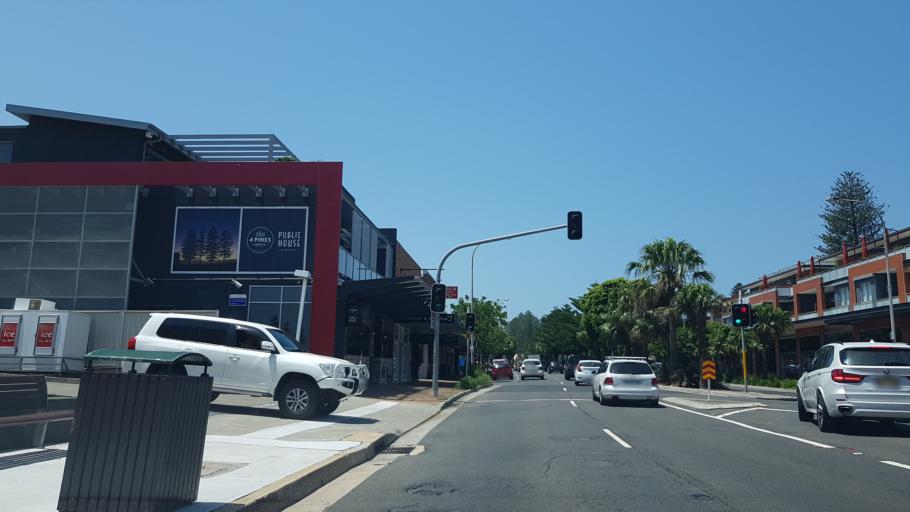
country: AU
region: New South Wales
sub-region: Pittwater
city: Newport
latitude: -33.6565
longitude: 151.3183
